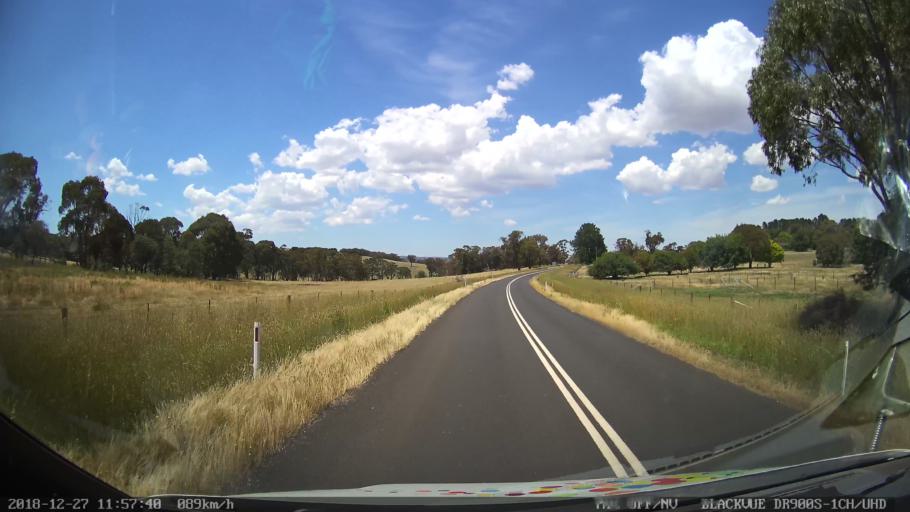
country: AU
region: New South Wales
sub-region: Blayney
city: Blayney
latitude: -33.7145
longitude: 149.3881
